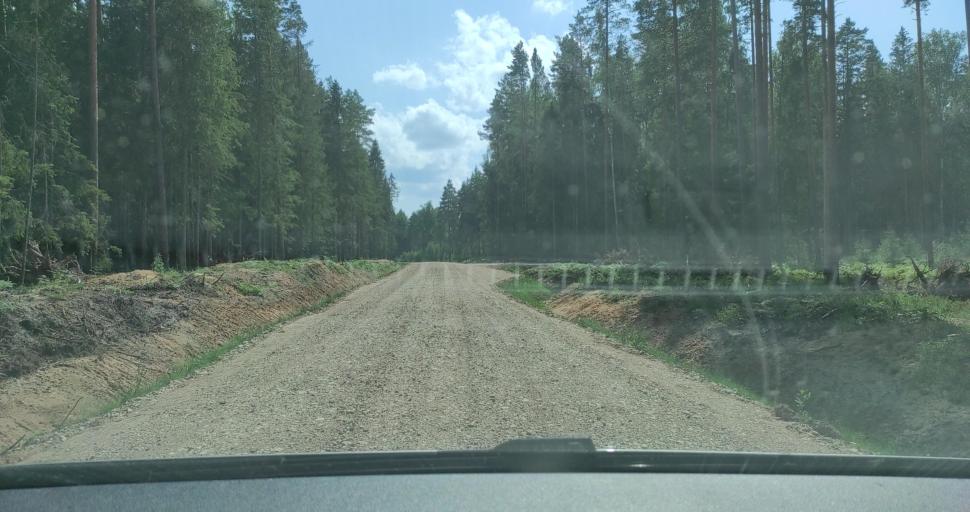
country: LV
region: Kuldigas Rajons
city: Kuldiga
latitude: 57.0659
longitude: 22.1927
